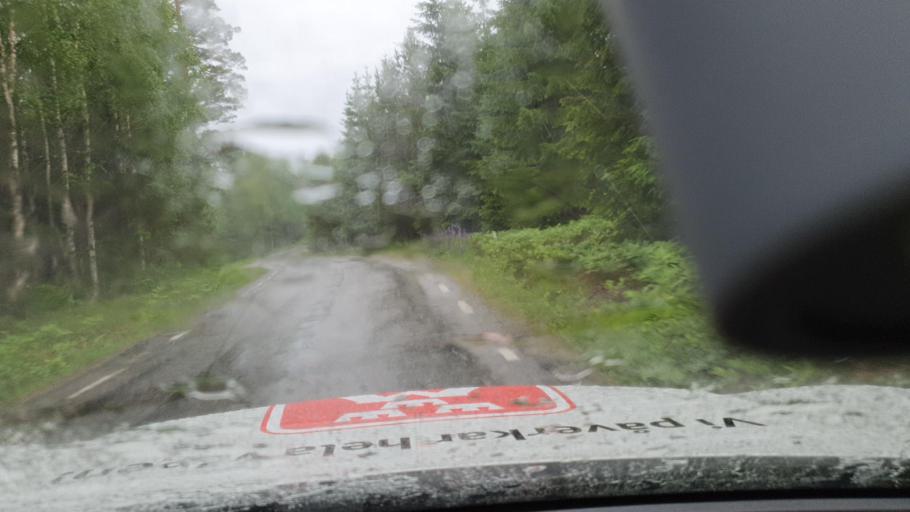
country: SE
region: Vaestra Goetaland
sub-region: Mariestads Kommun
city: Mariestad
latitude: 58.7722
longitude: 13.9323
